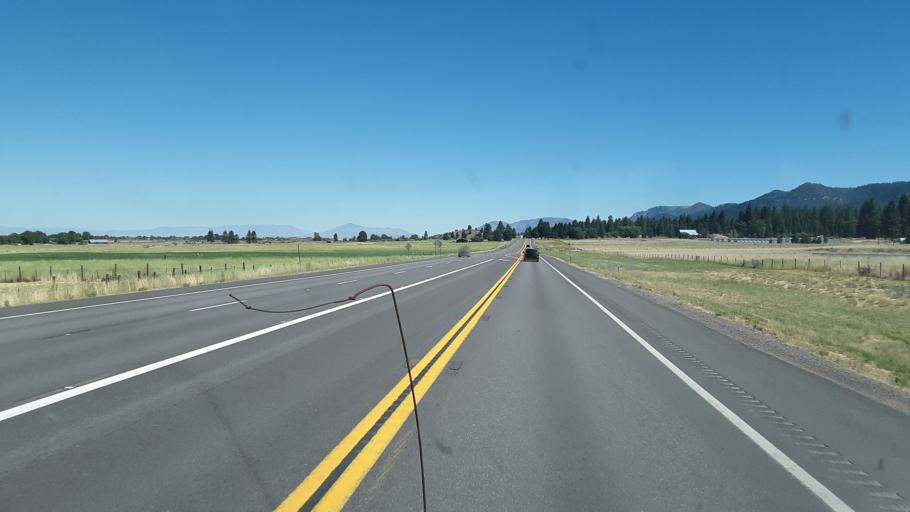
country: US
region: California
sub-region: Lassen County
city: Janesville
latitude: 40.3138
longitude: -120.5382
